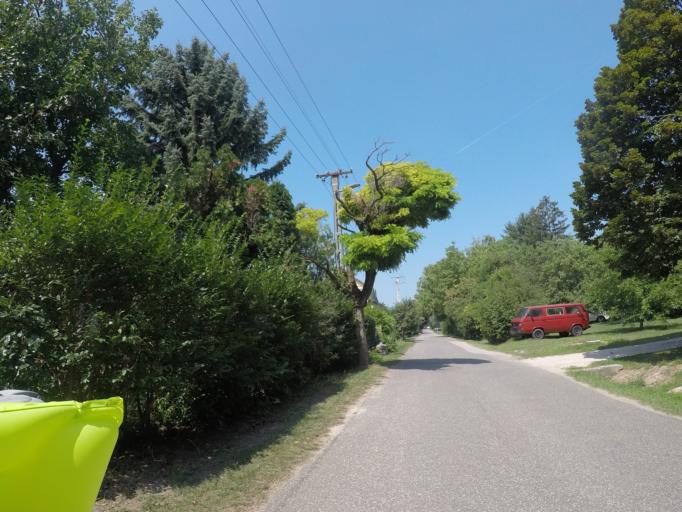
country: HU
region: Somogy
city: Balatonszabadi
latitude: 46.9332
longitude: 18.1235
